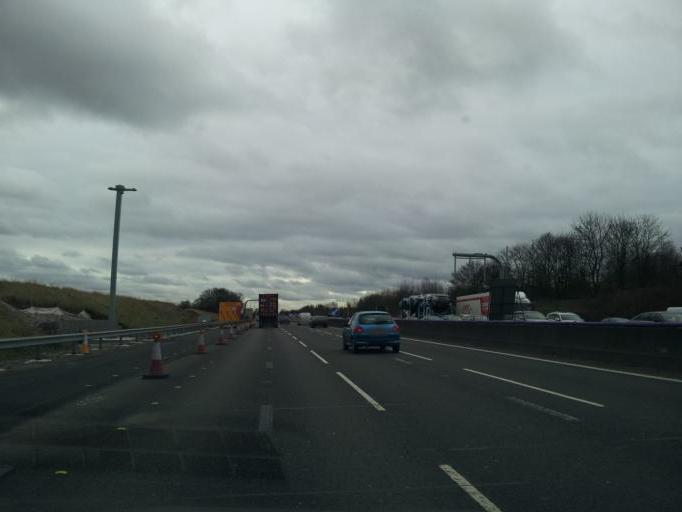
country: GB
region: England
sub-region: Staffordshire
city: Penkridge
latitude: 52.7162
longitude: -2.1018
